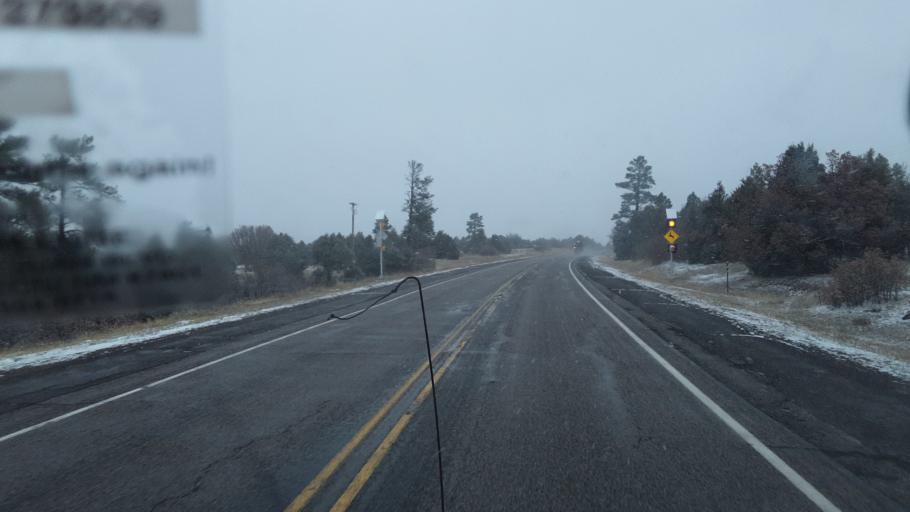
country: US
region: New Mexico
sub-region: Rio Arriba County
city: Chama
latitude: 36.8022
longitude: -106.5662
